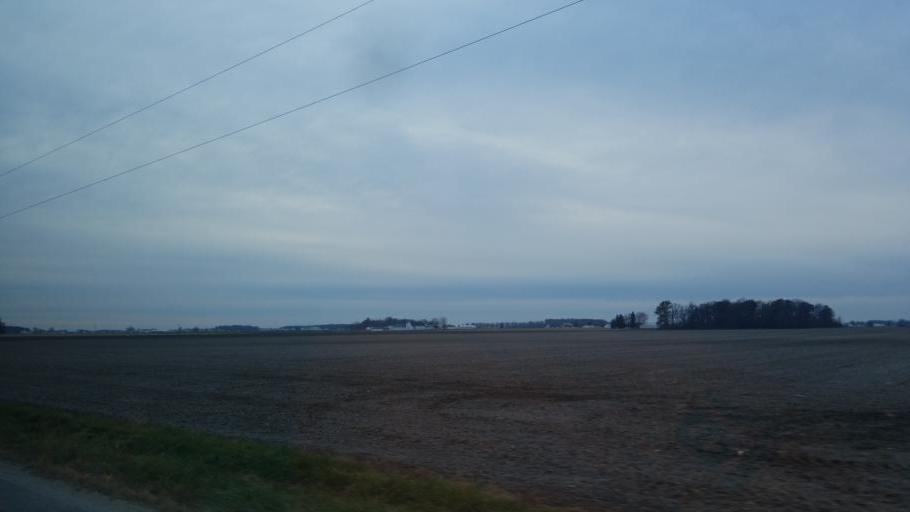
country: US
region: Indiana
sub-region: Adams County
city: Decatur
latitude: 40.7366
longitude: -84.8797
